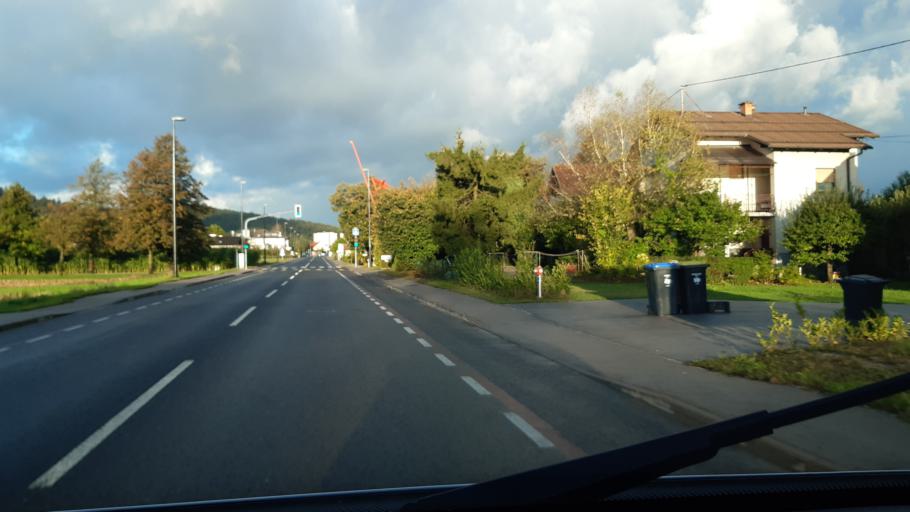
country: SI
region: Skofljica
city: Lavrica
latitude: 46.0451
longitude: 14.5654
